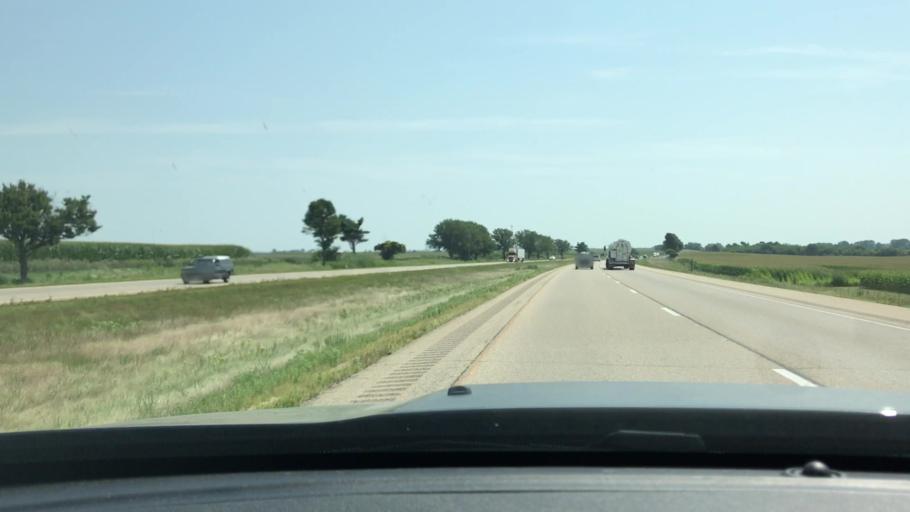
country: US
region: Illinois
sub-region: Bureau County
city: Depue
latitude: 41.4002
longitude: -89.3178
